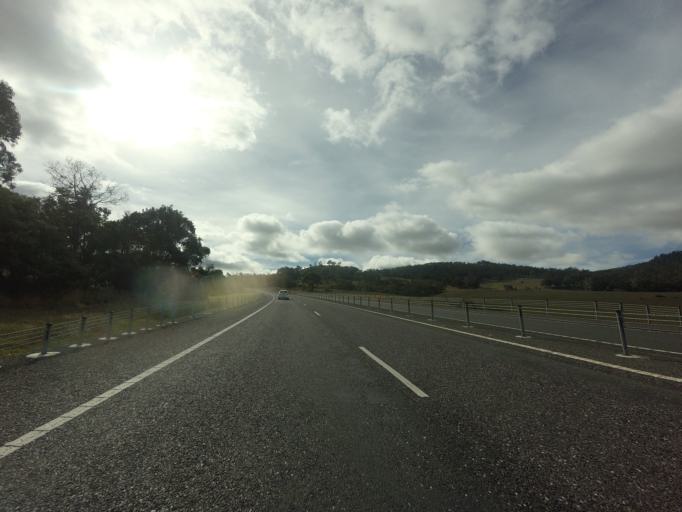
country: AU
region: Tasmania
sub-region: Brighton
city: Bridgewater
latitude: -42.4380
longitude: 147.2589
